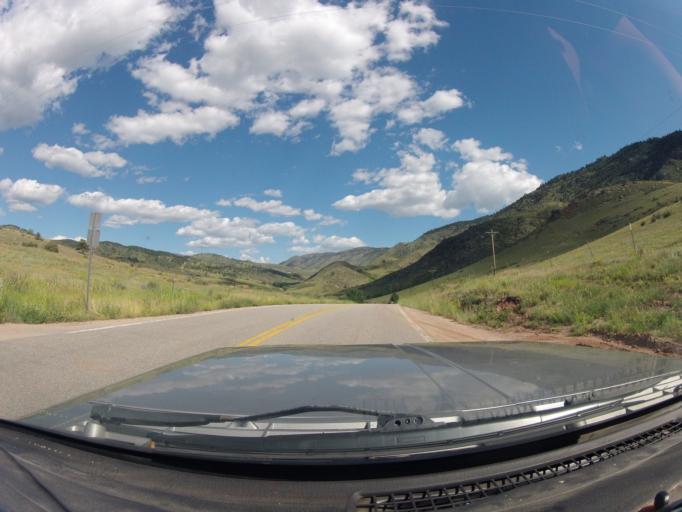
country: US
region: Colorado
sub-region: Larimer County
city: Laporte
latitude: 40.5329
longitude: -105.2706
